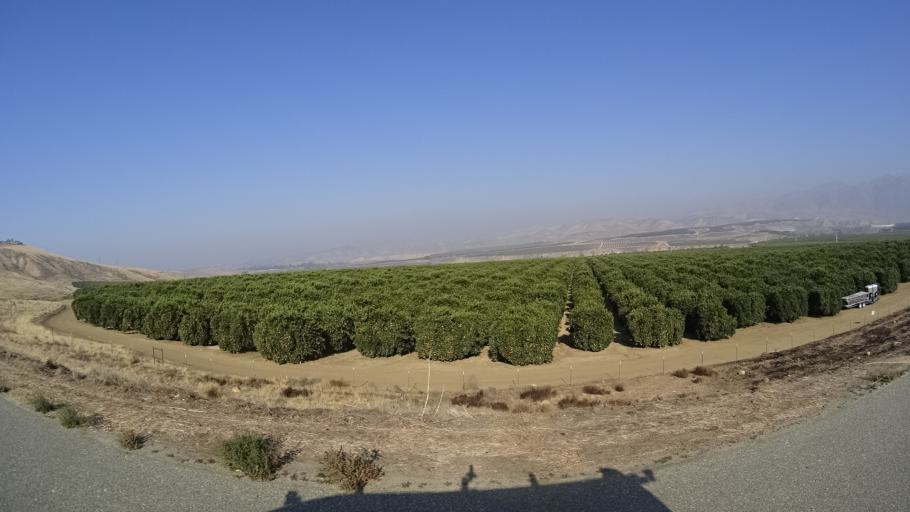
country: US
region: California
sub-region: Kern County
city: Lamont
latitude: 35.4155
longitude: -118.8347
